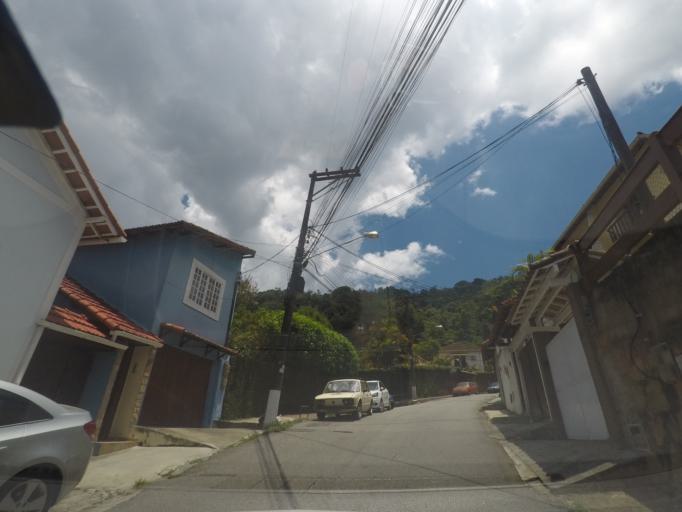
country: BR
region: Rio de Janeiro
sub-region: Petropolis
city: Petropolis
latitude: -22.5015
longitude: -43.1866
